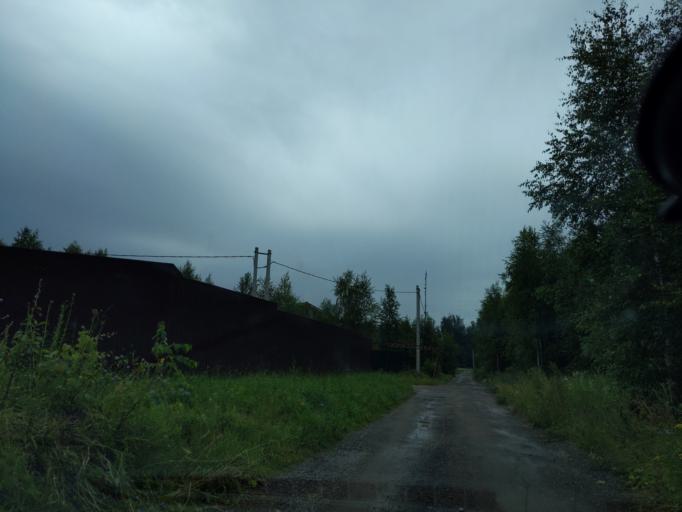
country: RU
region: Moskovskaya
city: Lugovaya
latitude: 56.0548
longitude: 37.4984
